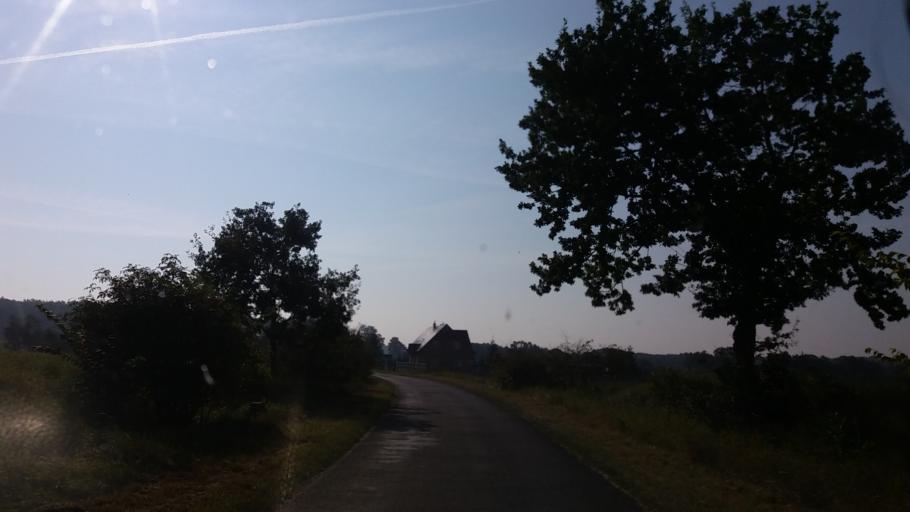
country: PL
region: West Pomeranian Voivodeship
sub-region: Powiat choszczenski
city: Pelczyce
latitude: 53.0018
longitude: 15.3620
